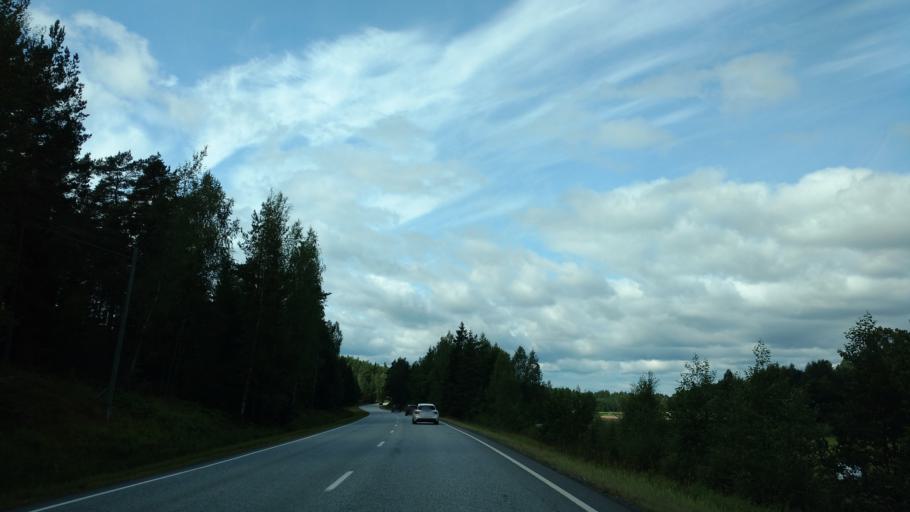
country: FI
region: Varsinais-Suomi
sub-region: Salo
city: Saerkisalo
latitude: 60.1778
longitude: 22.9293
